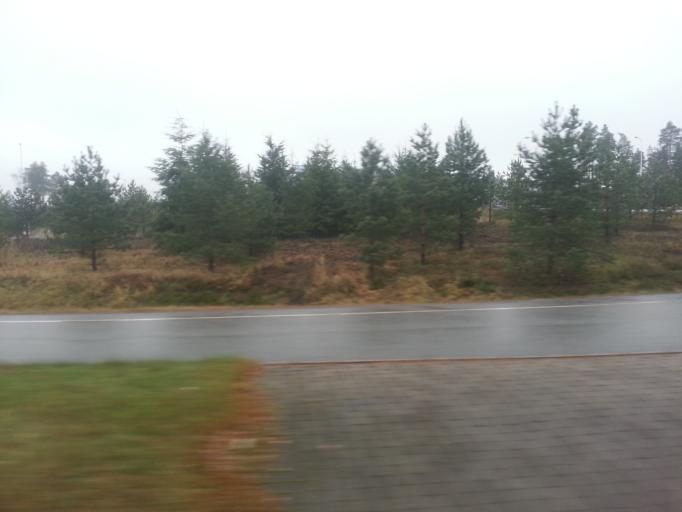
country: FI
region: Uusimaa
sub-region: Helsinki
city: Vantaa
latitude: 60.3080
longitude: 24.9641
